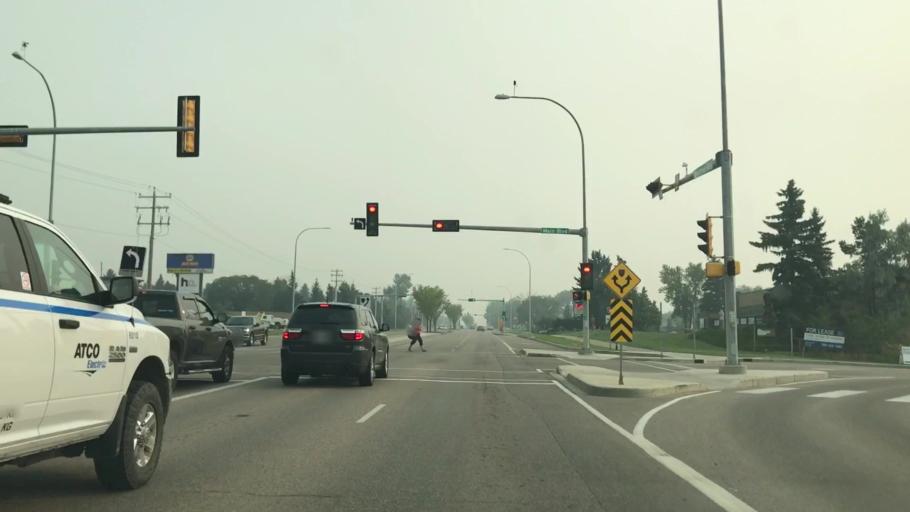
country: CA
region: Alberta
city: Sherwood Park
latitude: 53.5381
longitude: -113.3202
